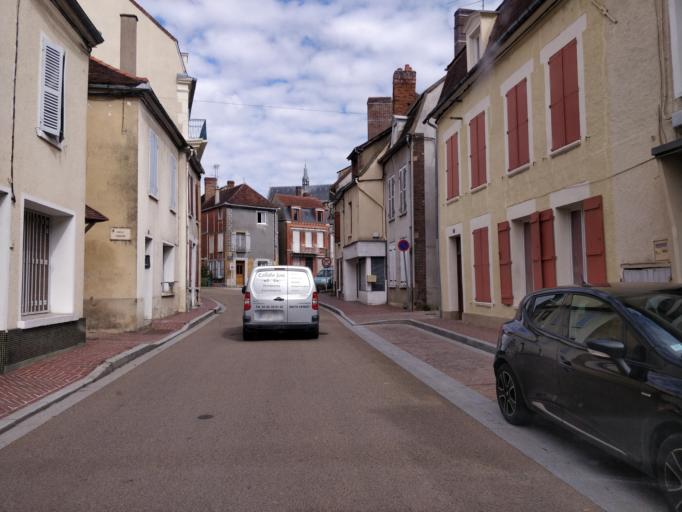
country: FR
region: Bourgogne
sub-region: Departement de l'Yonne
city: Saint-Florentin
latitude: 47.9991
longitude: 3.7274
